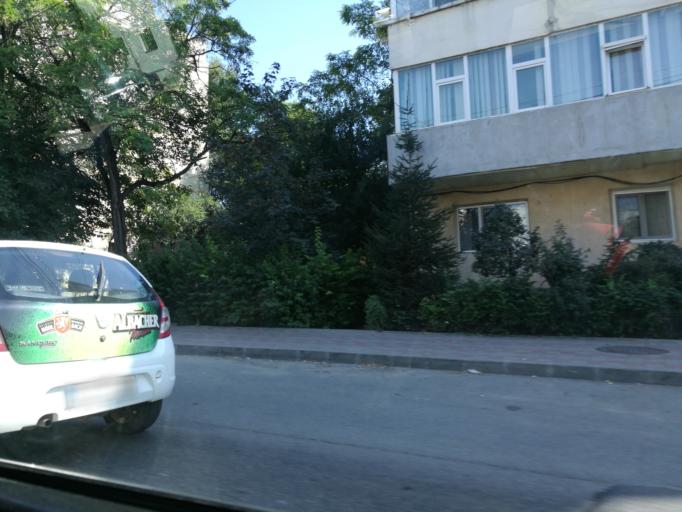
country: RO
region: Iasi
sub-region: Comuna Miroslava
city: Miroslava
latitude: 47.1734
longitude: 27.5481
